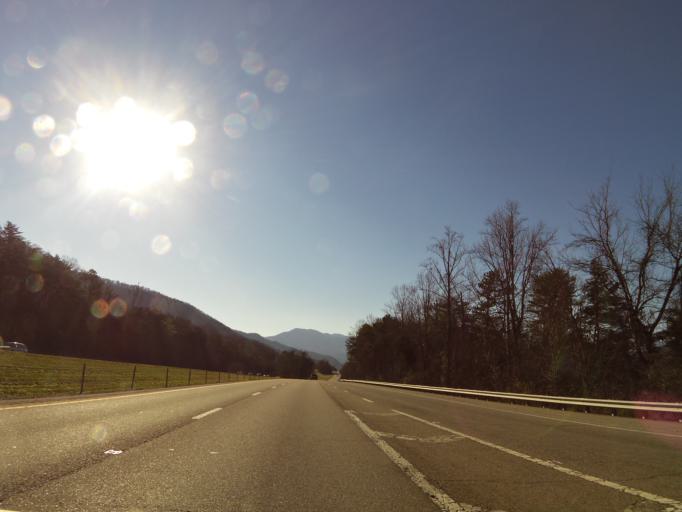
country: US
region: Tennessee
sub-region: Cocke County
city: Newport
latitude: 35.8756
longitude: -83.1860
